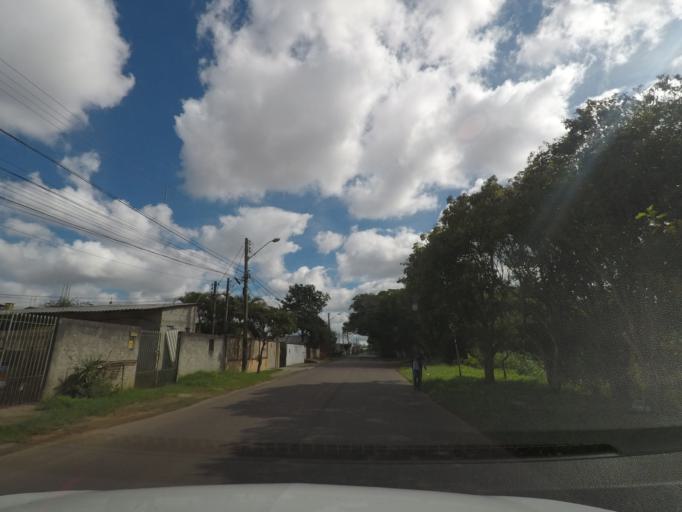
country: BR
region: Parana
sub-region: Curitiba
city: Curitiba
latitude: -25.4730
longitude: -49.2451
